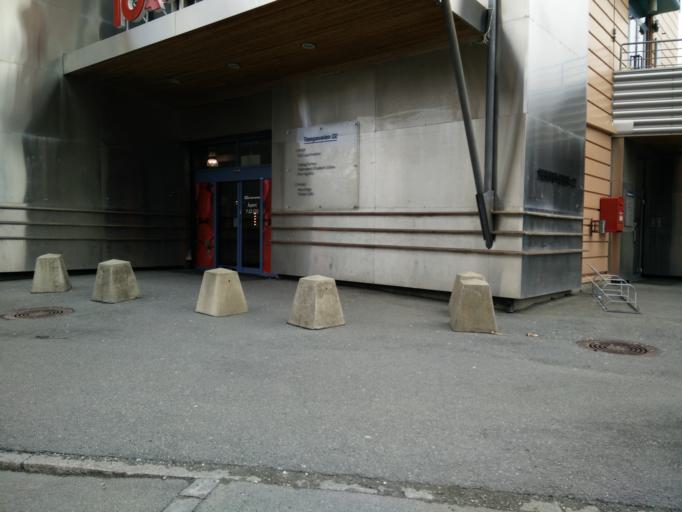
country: NO
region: Sor-Trondelag
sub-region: Trondheim
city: Trondheim
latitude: 63.4073
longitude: 10.3970
